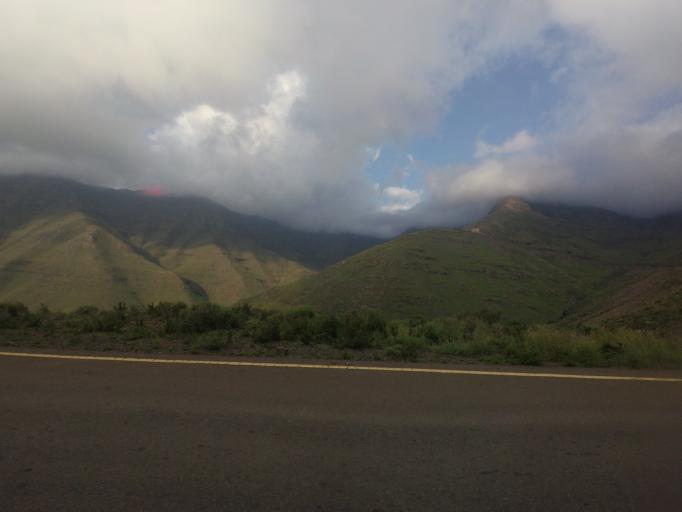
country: LS
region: Butha-Buthe
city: Butha-Buthe
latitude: -29.0680
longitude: 28.3707
